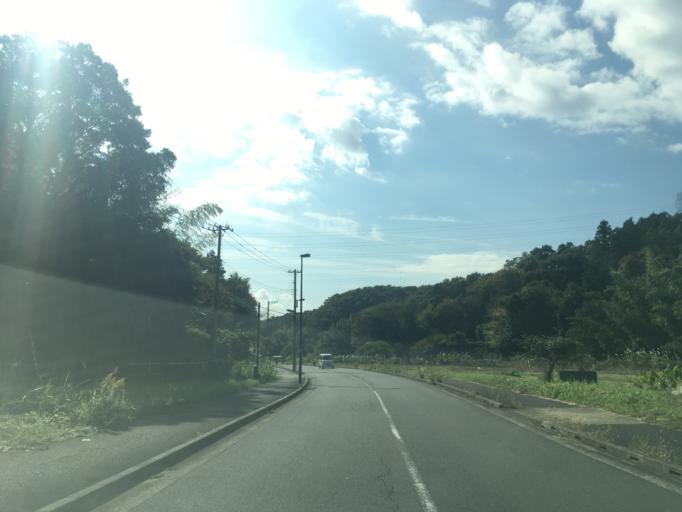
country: JP
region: Tokyo
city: Hino
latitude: 35.6050
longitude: 139.4081
